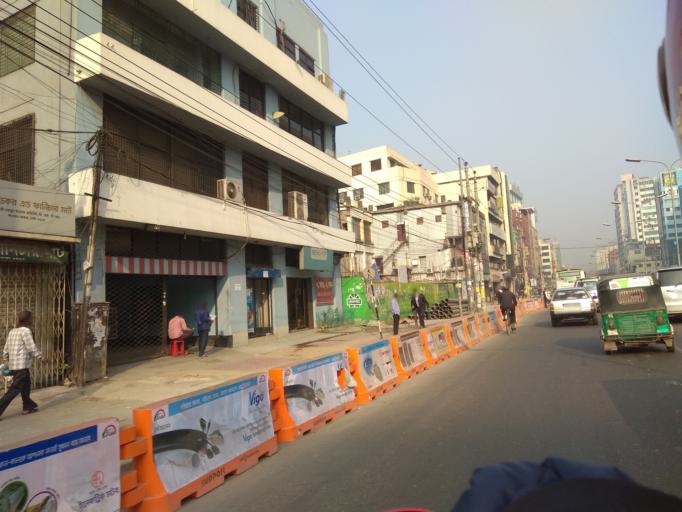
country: BD
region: Dhaka
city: Azimpur
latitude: 23.7520
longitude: 90.3924
